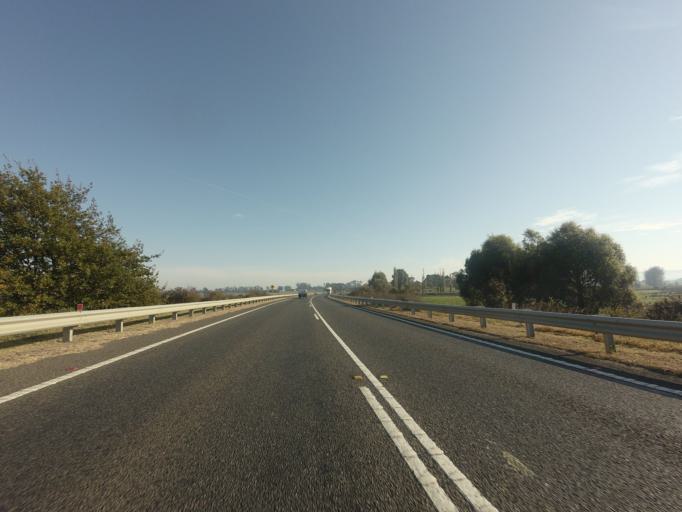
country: AU
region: Tasmania
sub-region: Northern Midlands
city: Longford
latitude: -41.5804
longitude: 147.1062
